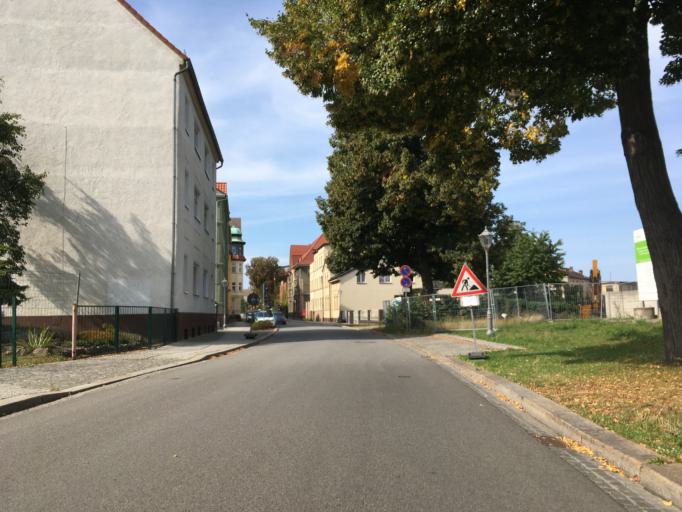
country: DE
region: Brandenburg
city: Guben
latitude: 51.9562
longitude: 14.7147
